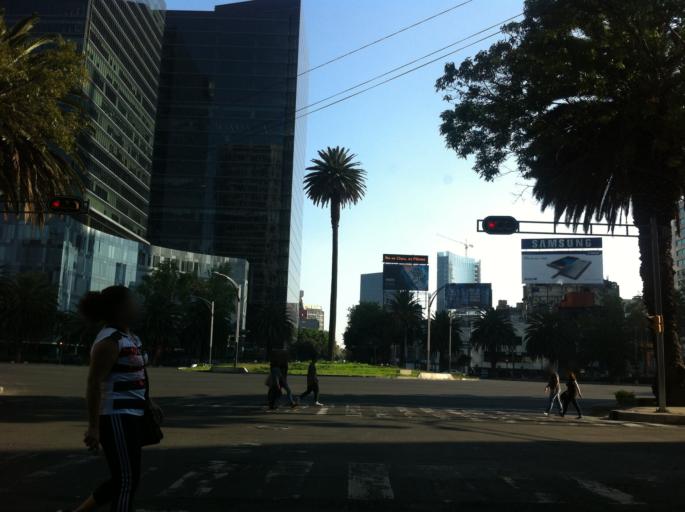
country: MX
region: Mexico City
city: Cuauhtemoc
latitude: 19.4296
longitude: -99.1641
